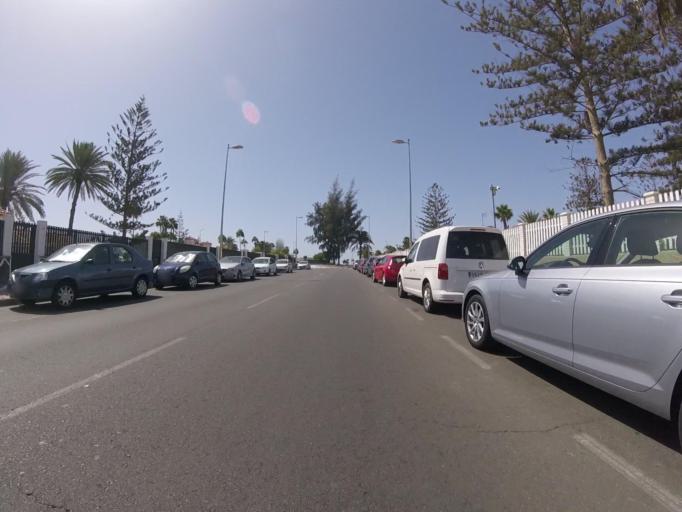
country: ES
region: Canary Islands
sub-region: Provincia de Las Palmas
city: Playa del Ingles
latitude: 27.7574
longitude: -15.5809
